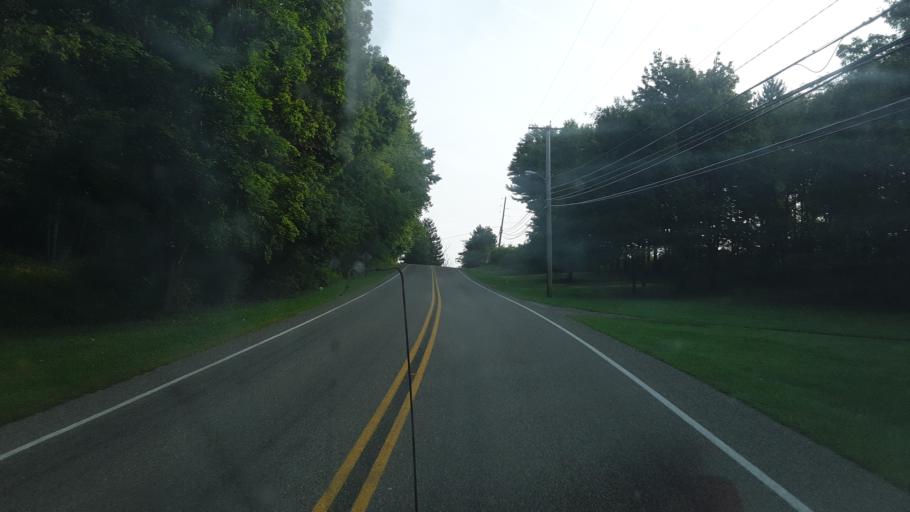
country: US
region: Pennsylvania
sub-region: Jefferson County
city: Punxsutawney
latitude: 40.9646
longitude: -79.0311
